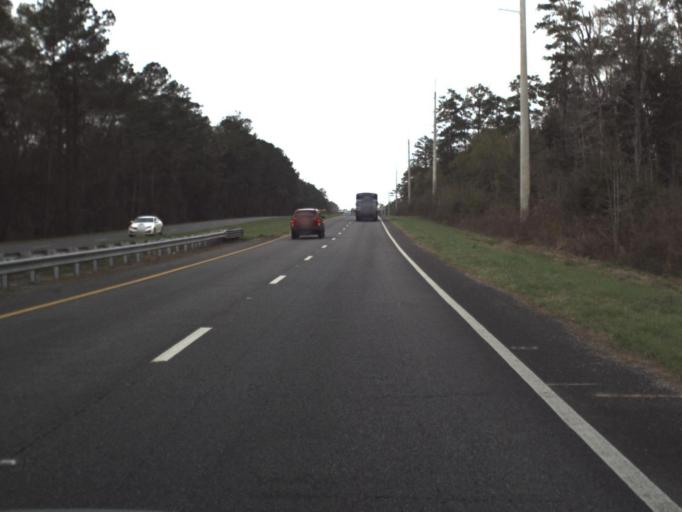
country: US
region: Florida
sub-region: Leon County
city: Woodville
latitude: 30.4085
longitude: -84.0650
